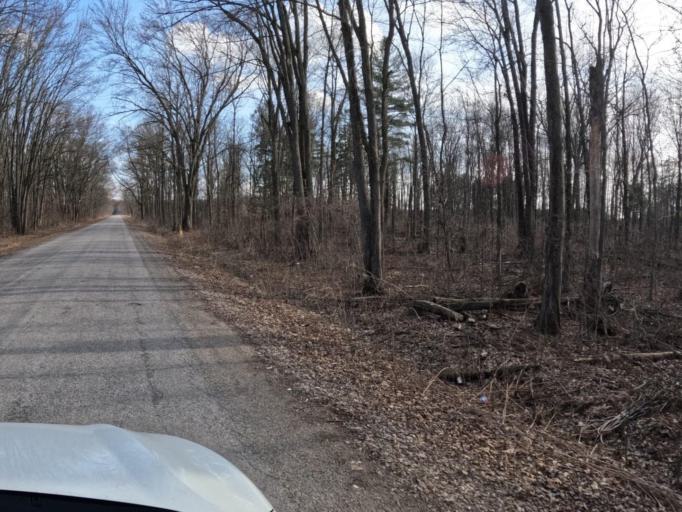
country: CA
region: Ontario
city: Brant
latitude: 43.0006
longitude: -80.4122
